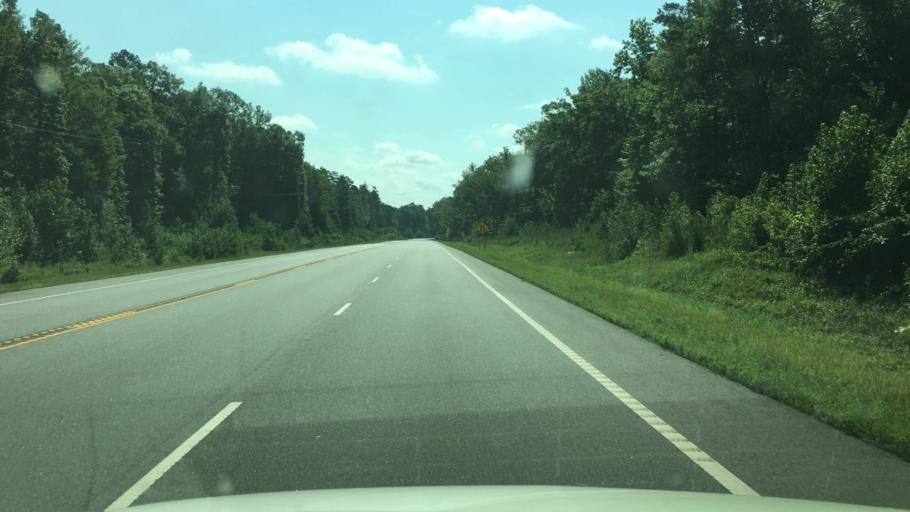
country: US
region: Arkansas
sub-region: Garland County
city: Rockwell
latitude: 34.5179
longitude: -93.3090
